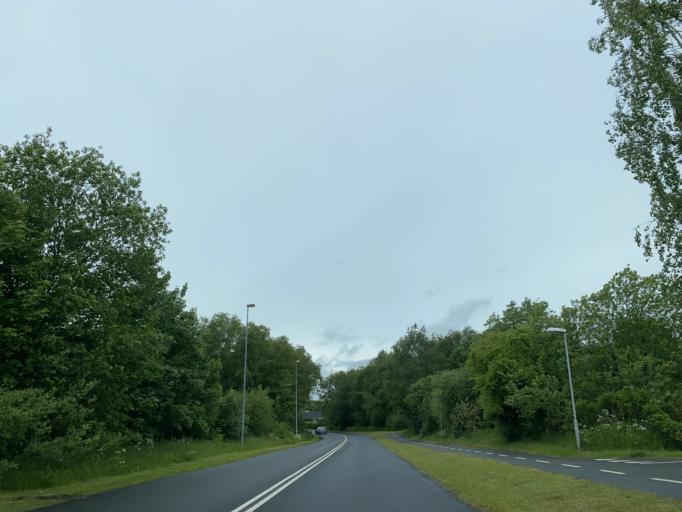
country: DK
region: Central Jutland
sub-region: Favrskov Kommune
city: Hammel
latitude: 56.2440
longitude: 9.8678
